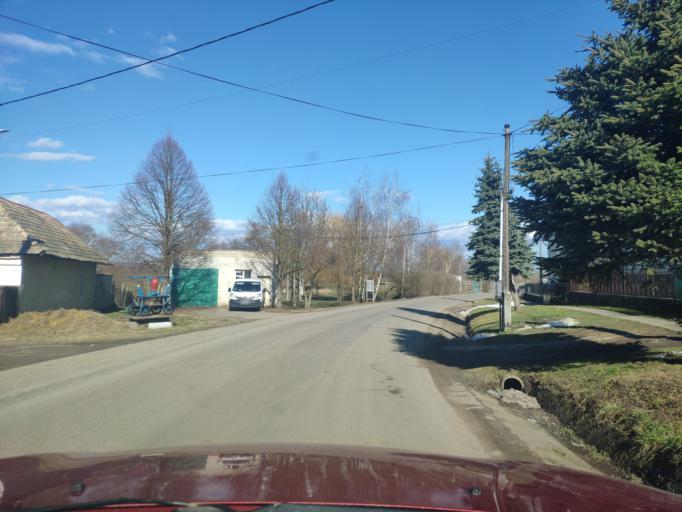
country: SK
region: Banskobystricky
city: Rimavska Sobota
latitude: 48.2775
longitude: 20.1147
